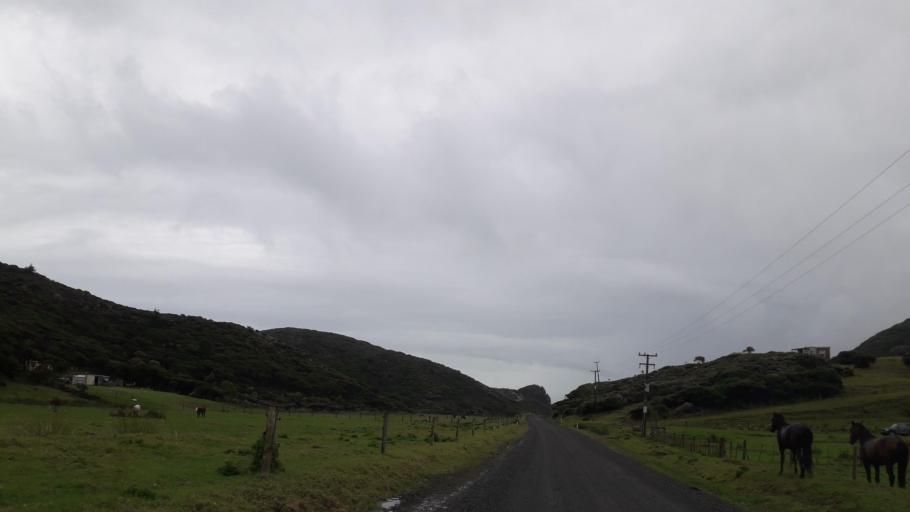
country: NZ
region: Northland
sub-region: Far North District
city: Ahipara
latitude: -35.4405
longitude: 173.2960
